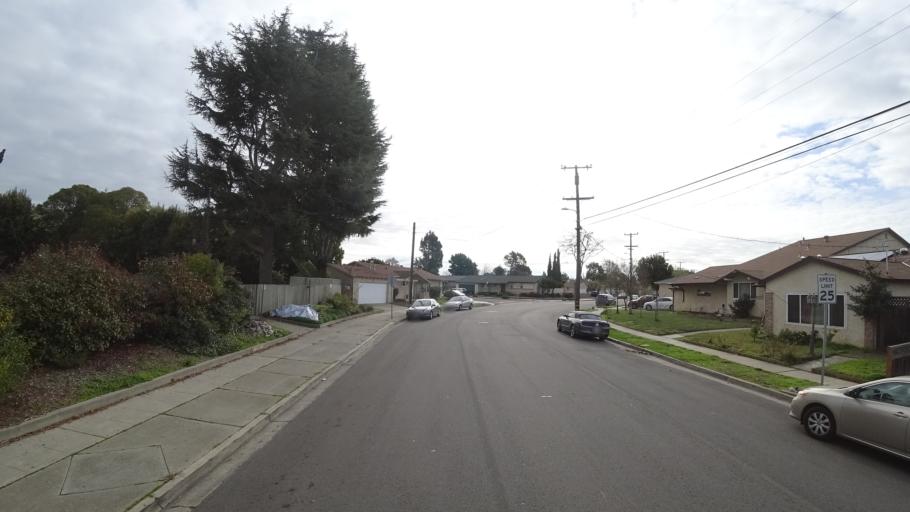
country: US
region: California
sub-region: Alameda County
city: Union City
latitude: 37.6166
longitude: -122.0366
